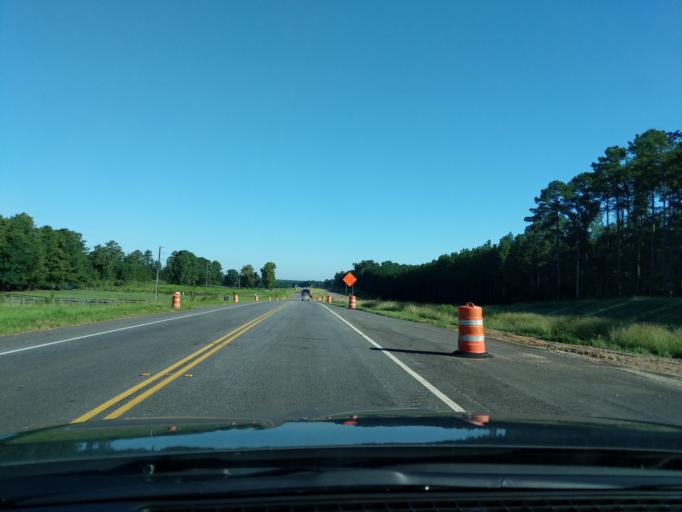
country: US
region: Georgia
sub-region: McDuffie County
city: Thomson
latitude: 33.5620
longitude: -82.5156
